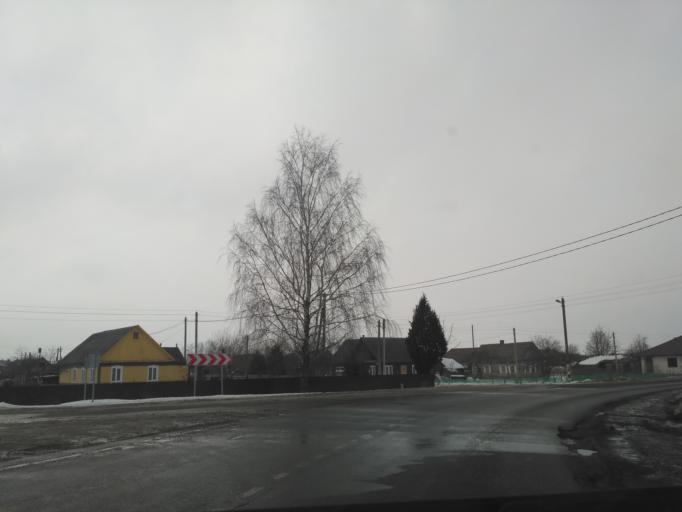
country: BY
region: Minsk
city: Horad Smalyavichy
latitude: 54.0258
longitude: 28.0649
